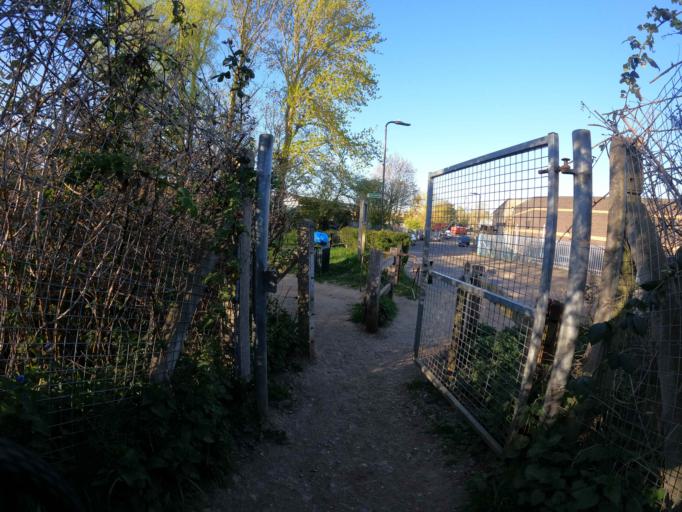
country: GB
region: England
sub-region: Greater London
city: Isleworth
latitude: 51.4998
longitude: -0.3407
